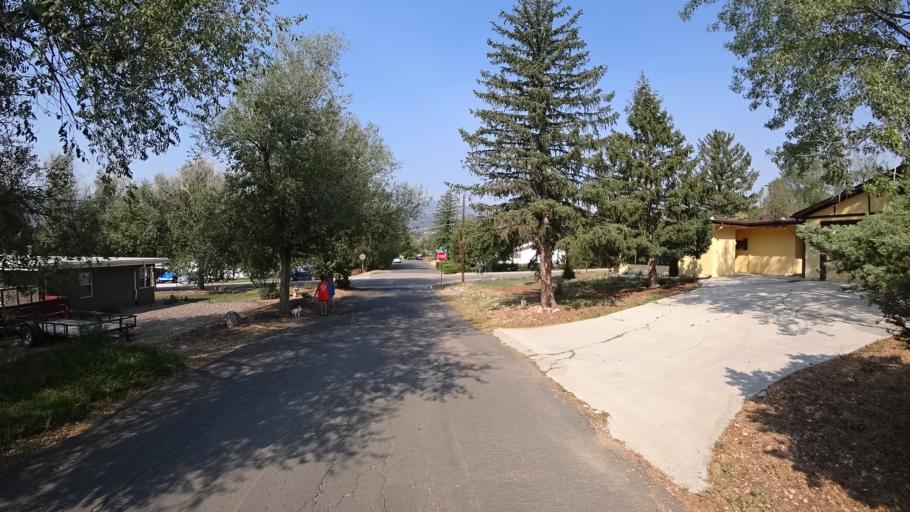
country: US
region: Colorado
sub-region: El Paso County
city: Colorado Springs
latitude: 38.8119
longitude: -104.8346
